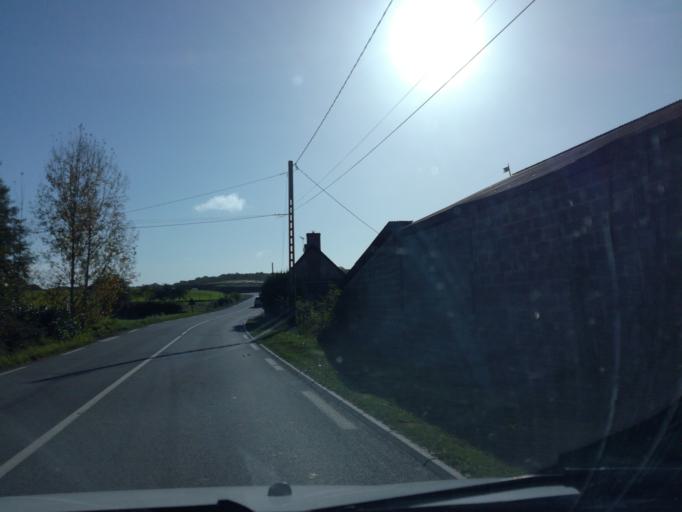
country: FR
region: Brittany
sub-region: Departement d'Ille-et-Vilaine
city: Martigne-Ferchaud
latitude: 47.8005
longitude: -1.2791
